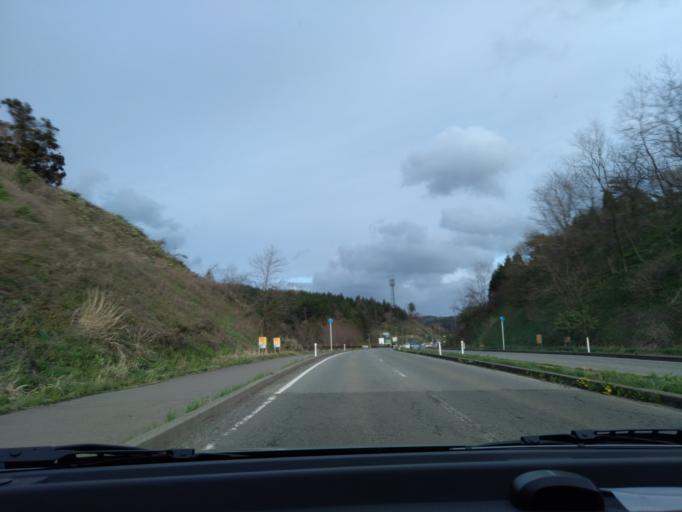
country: JP
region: Akita
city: Akita
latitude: 39.7516
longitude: 140.1195
